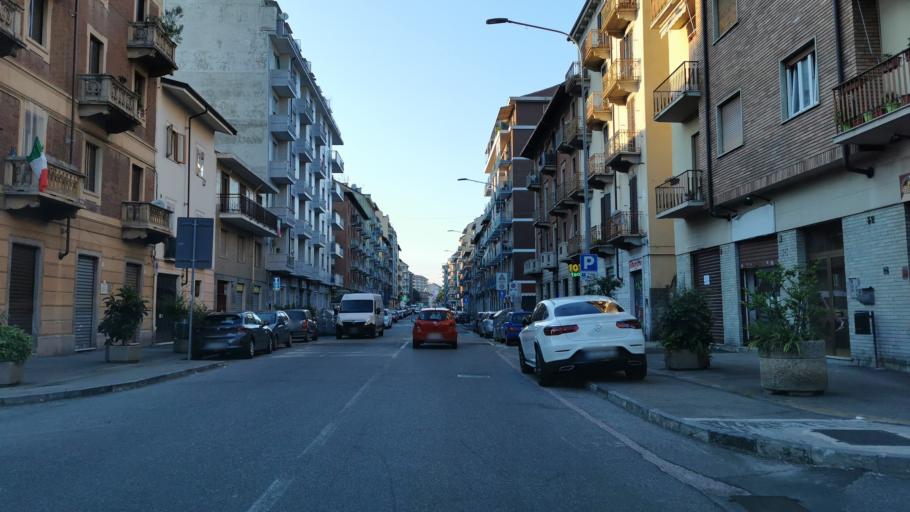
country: IT
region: Piedmont
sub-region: Provincia di Torino
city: Turin
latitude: 45.0961
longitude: 7.6938
